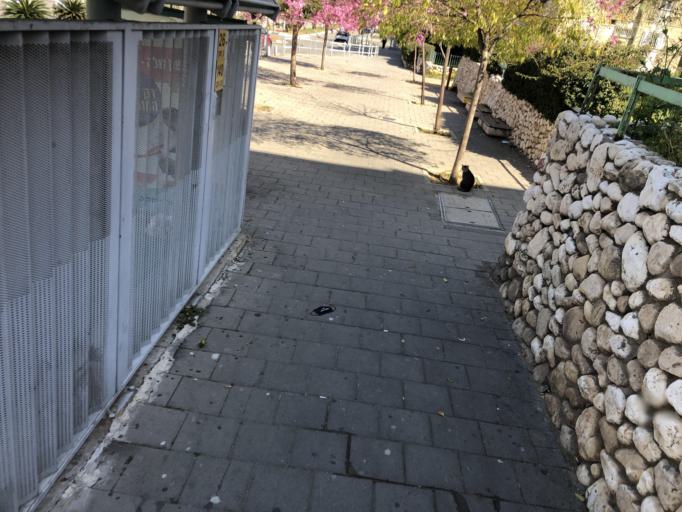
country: IL
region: Tel Aviv
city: Bat Yam
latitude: 32.0091
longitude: 34.7569
